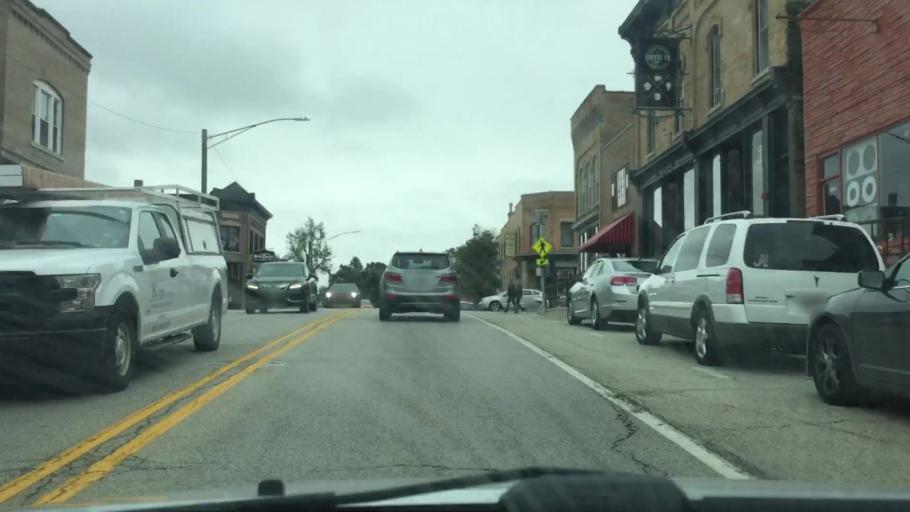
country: US
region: Illinois
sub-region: McHenry County
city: Richmond
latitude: 42.4764
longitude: -88.3061
